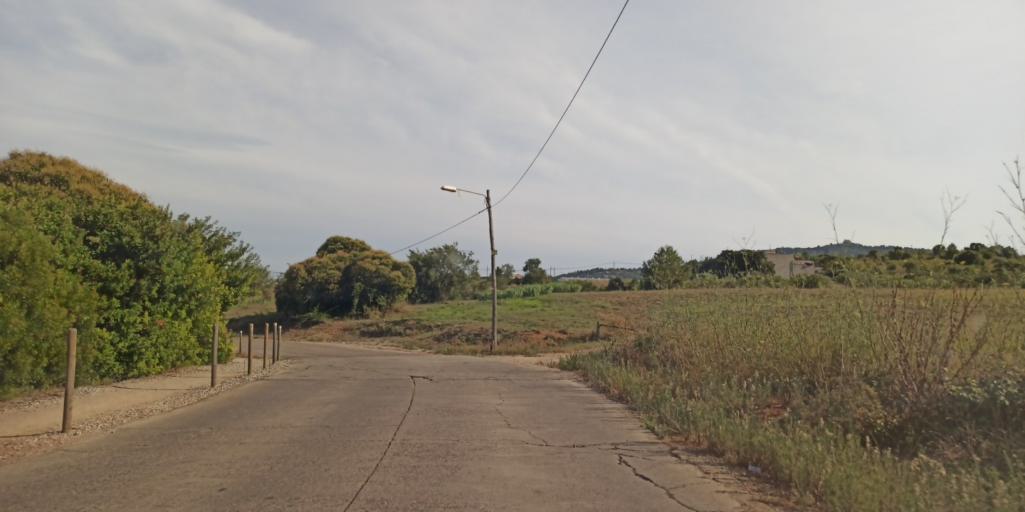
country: ES
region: Catalonia
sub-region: Provincia de Barcelona
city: Santa Coloma de Cervello
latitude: 41.3616
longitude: 2.0239
